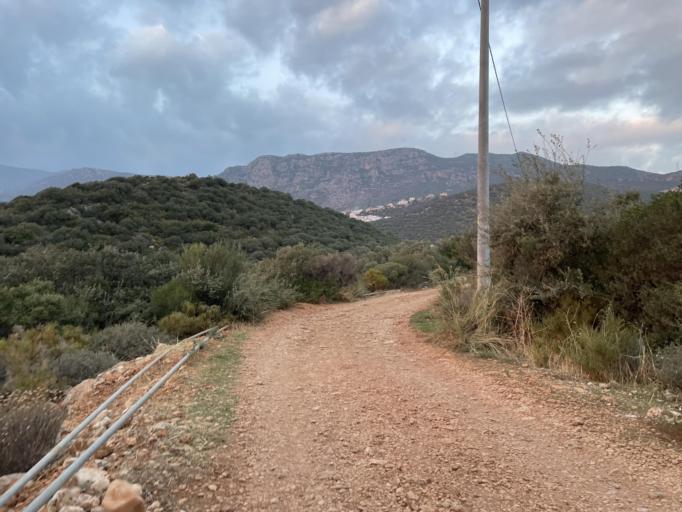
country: TR
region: Antalya
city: Kas
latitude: 36.1855
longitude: 29.6521
